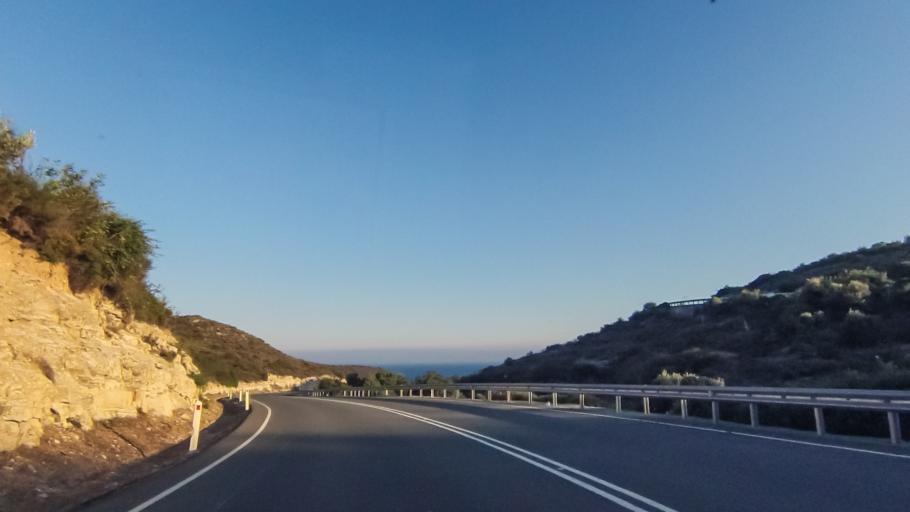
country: CY
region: Limassol
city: Sotira
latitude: 34.6746
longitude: 32.8160
